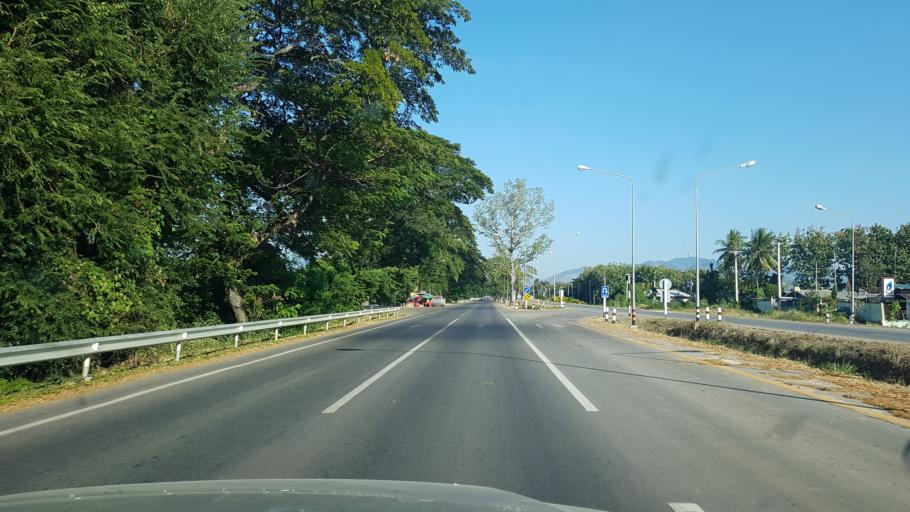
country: TH
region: Phetchabun
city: Lom Sak
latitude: 16.7266
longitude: 101.2469
